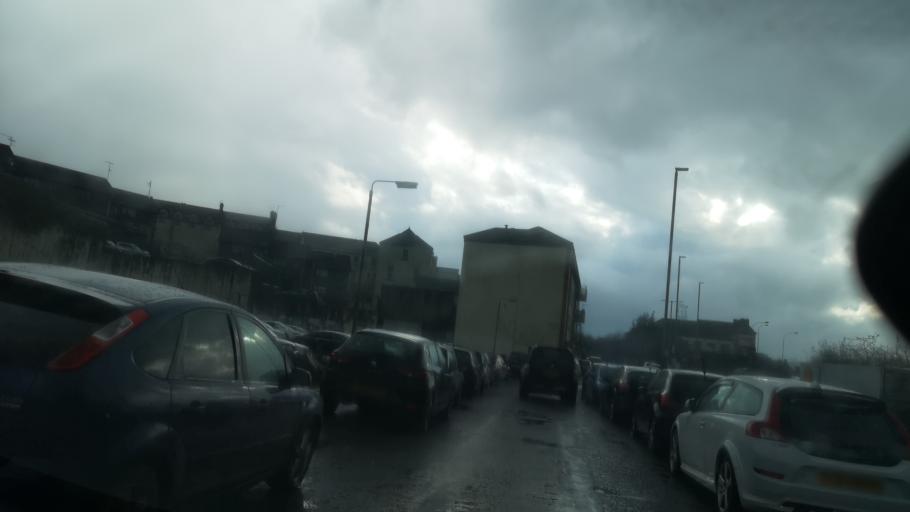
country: GB
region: Northern Ireland
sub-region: Newry and Mourne District
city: Newry
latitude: 54.1755
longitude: -6.3359
